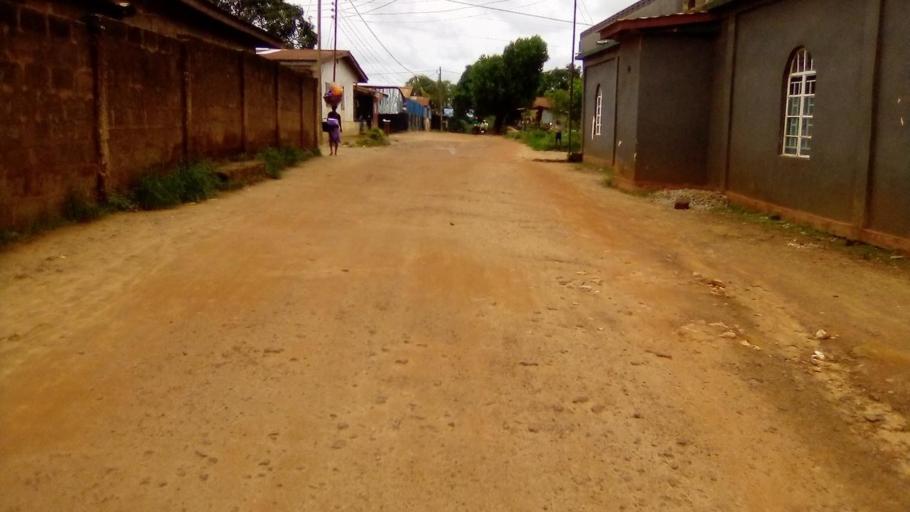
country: SL
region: Southern Province
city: Bo
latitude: 7.9438
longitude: -11.7399
